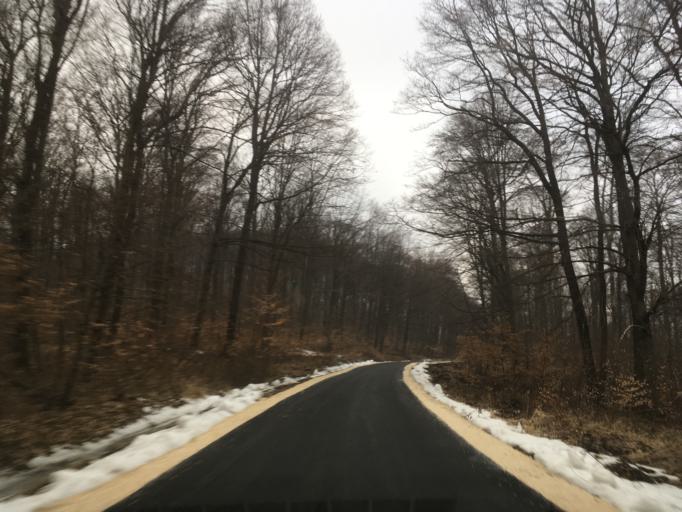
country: HU
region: Komarom-Esztergom
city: Kesztolc
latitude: 47.7254
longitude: 18.8564
